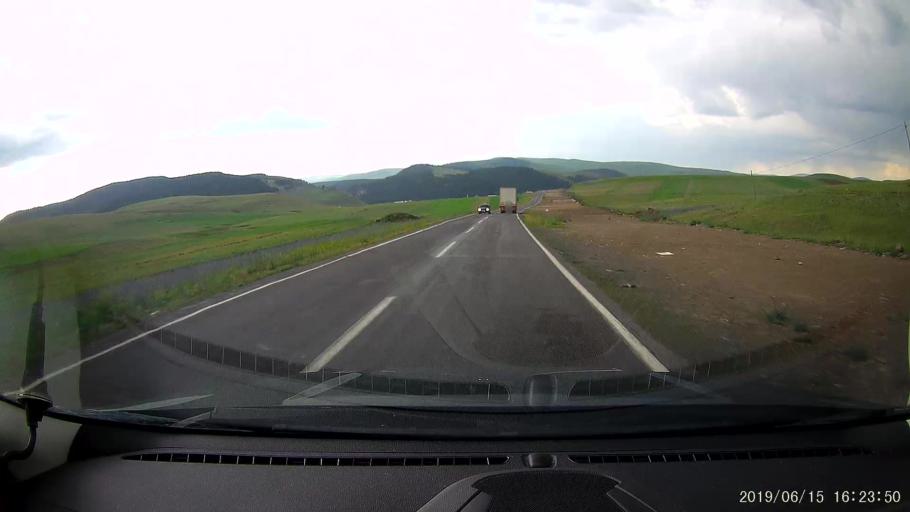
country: TR
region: Ardahan
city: Hanak
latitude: 41.1732
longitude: 42.8664
